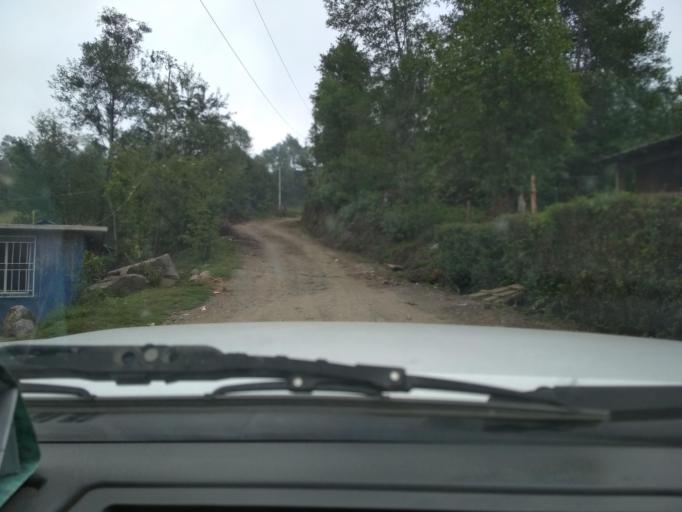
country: MX
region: Veracruz
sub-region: La Perla
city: Chilapa
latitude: 19.0003
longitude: -97.1688
